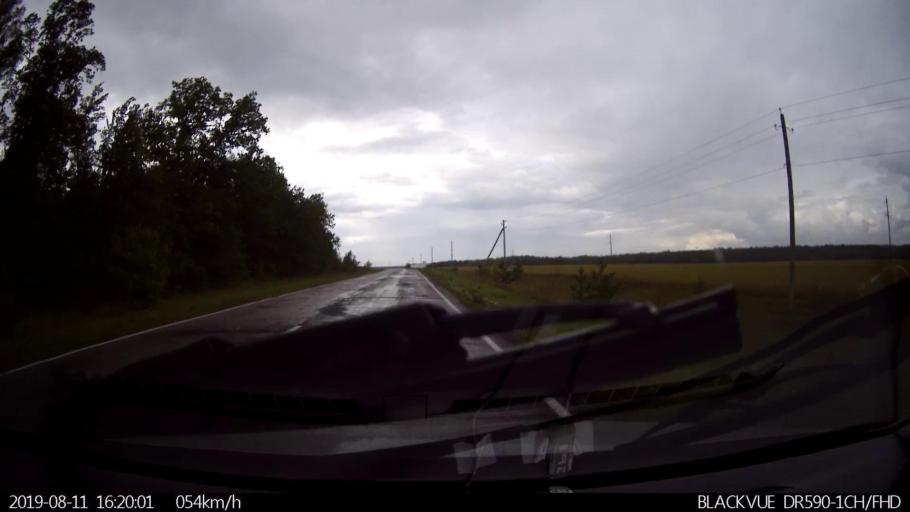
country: RU
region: Ulyanovsk
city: Mayna
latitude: 54.0685
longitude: 47.6048
